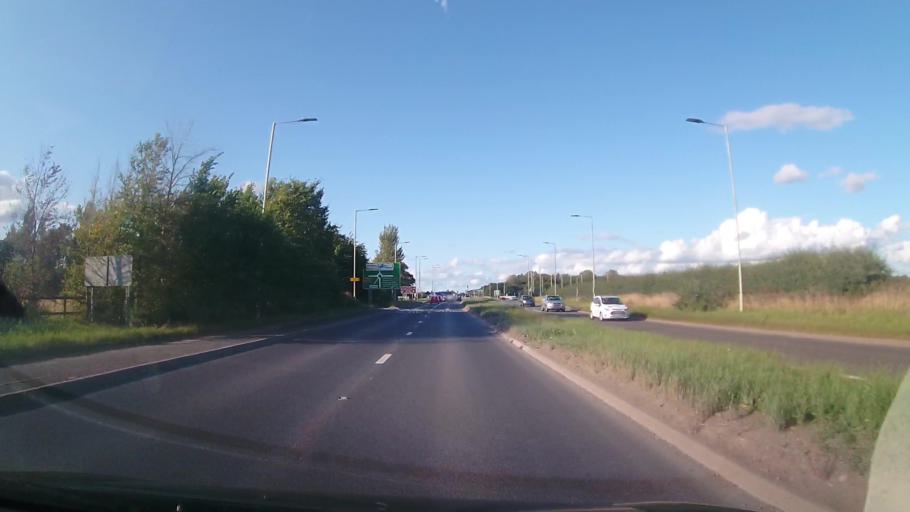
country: GB
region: England
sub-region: Shropshire
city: Bayston Hill
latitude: 52.6804
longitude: -2.7593
